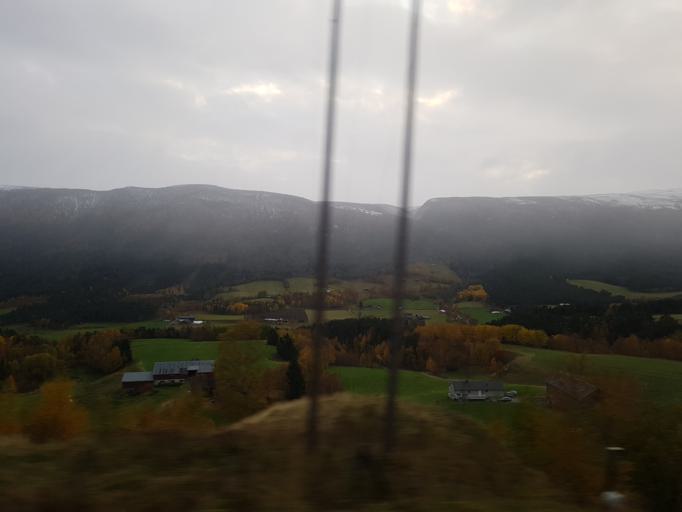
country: NO
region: Oppland
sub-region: Dovre
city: Dombas
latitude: 62.0320
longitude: 9.1749
